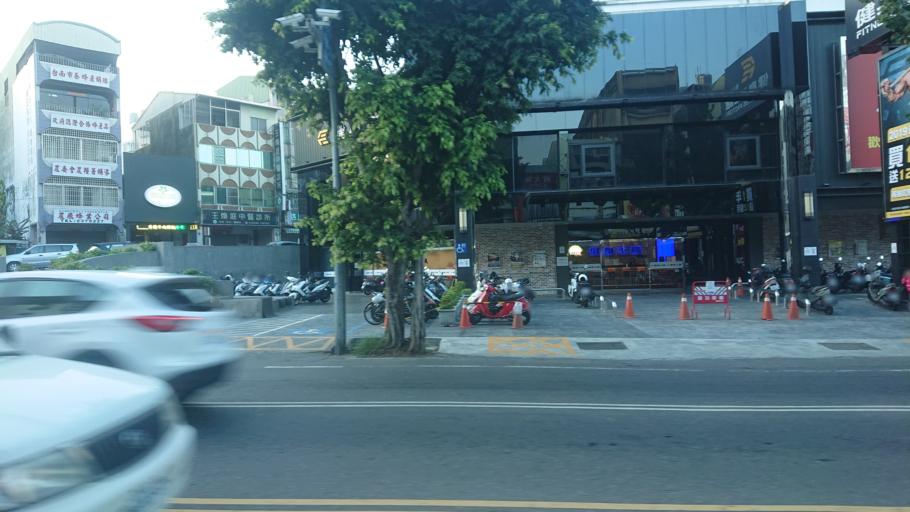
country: TW
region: Taiwan
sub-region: Tainan
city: Tainan
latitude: 23.0095
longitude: 120.2235
